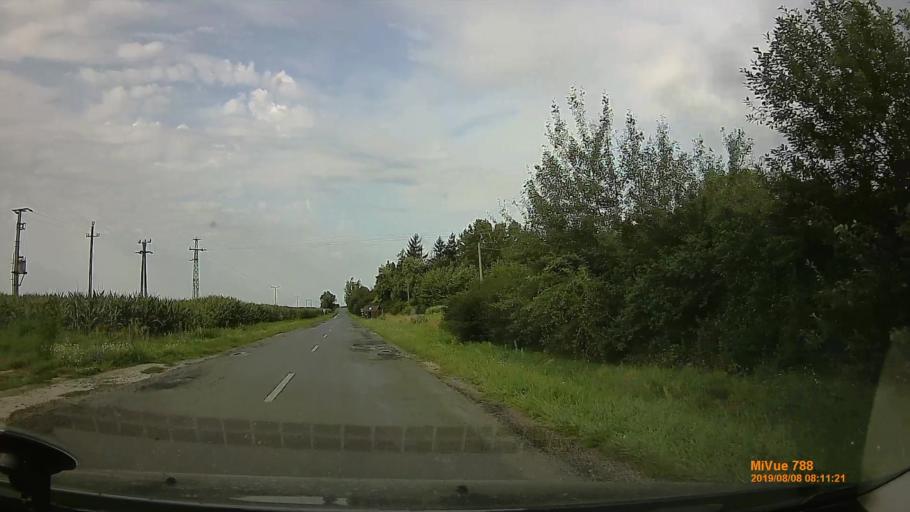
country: HU
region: Zala
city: Murakeresztur
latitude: 46.4236
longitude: 16.8820
